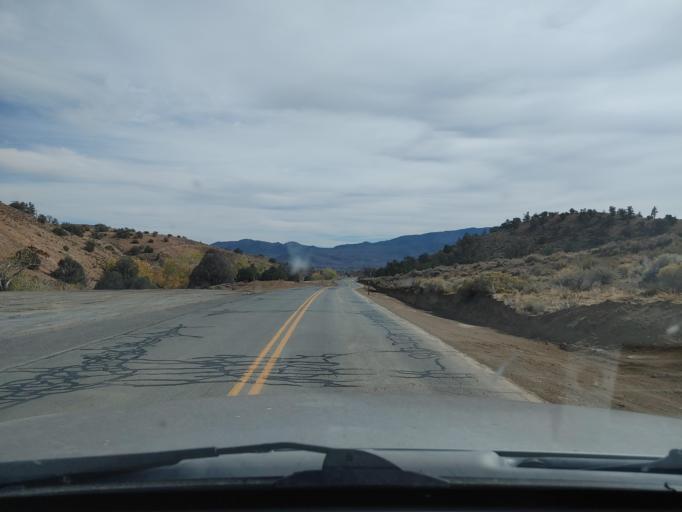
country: US
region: Nevada
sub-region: Storey County
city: Virginia City
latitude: 39.3110
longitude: -119.5760
